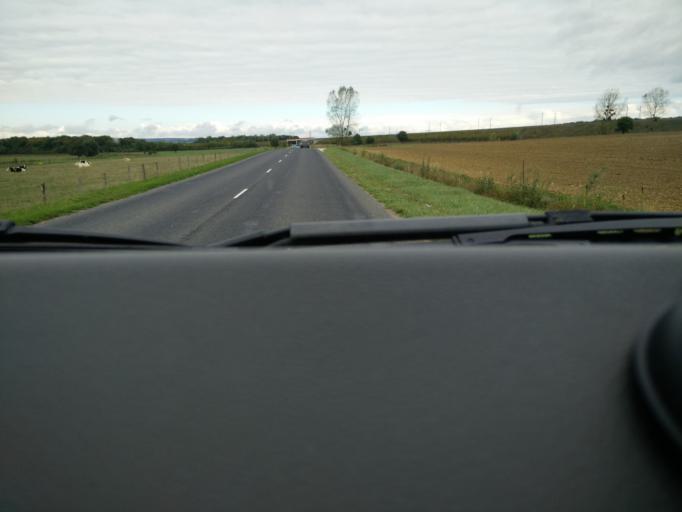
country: FR
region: Lorraine
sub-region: Departement de la Meuse
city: Vigneulles-les-Hattonchatel
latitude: 48.9675
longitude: 5.8135
